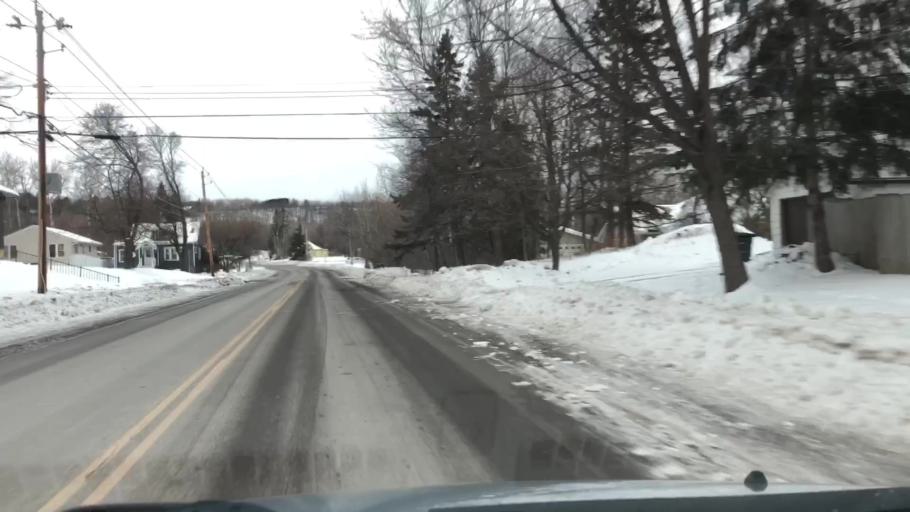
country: US
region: Minnesota
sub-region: Saint Louis County
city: Arnold
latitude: 46.8346
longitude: -92.0368
